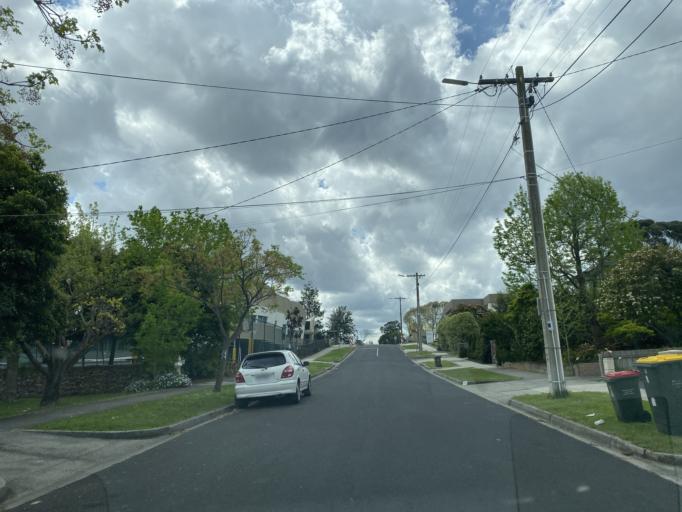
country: AU
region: Victoria
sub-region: Whitehorse
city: Burwood
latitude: -37.8531
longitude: 145.1262
